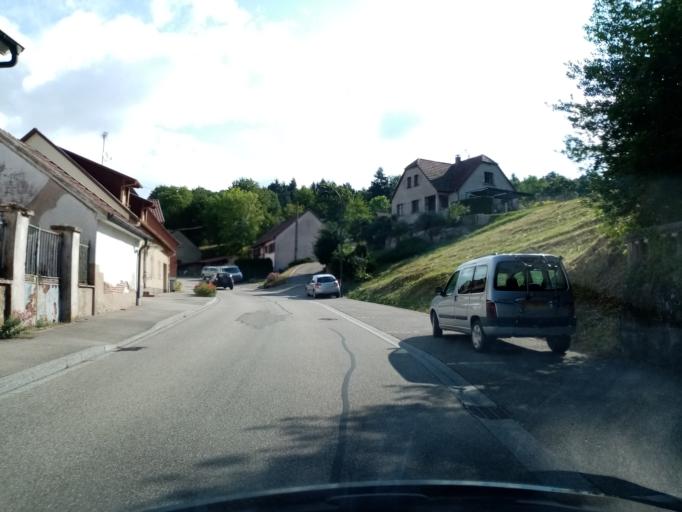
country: FR
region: Alsace
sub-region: Departement du Bas-Rhin
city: Ville
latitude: 48.3391
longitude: 7.3626
